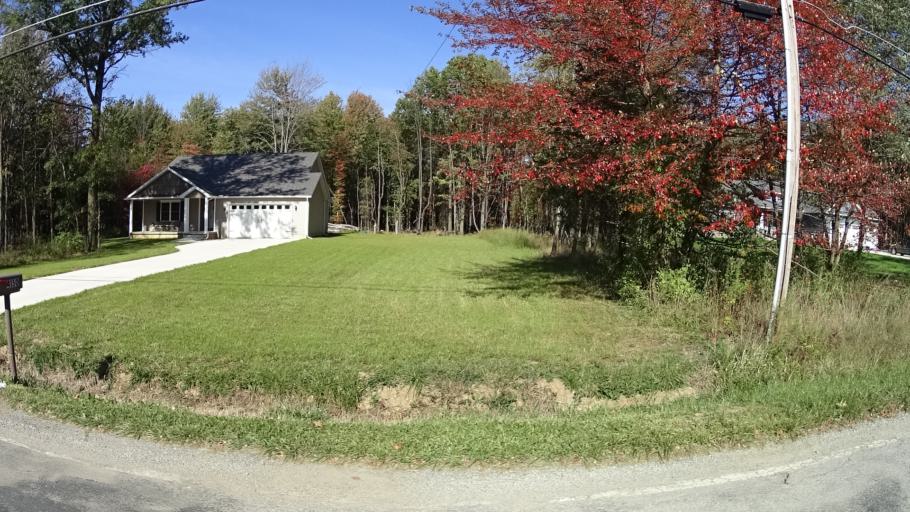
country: US
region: Ohio
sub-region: Lorain County
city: Vermilion-on-the-Lake
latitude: 41.4122
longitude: -82.3327
